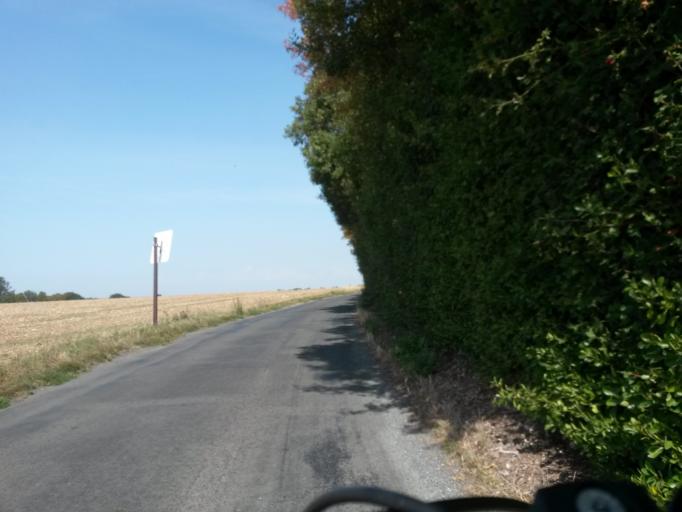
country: FR
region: Poitou-Charentes
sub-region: Departement de la Charente-Maritime
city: Puilboreau
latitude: 46.1870
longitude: -1.1349
